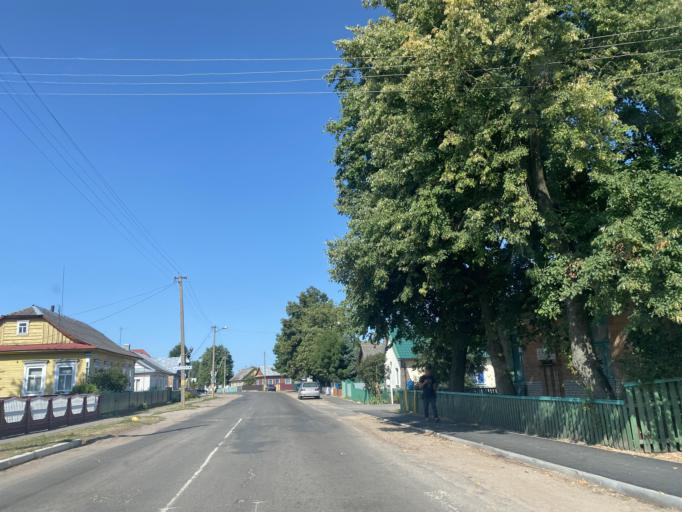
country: BY
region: Brest
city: Ivanava
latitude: 52.3168
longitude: 25.6075
